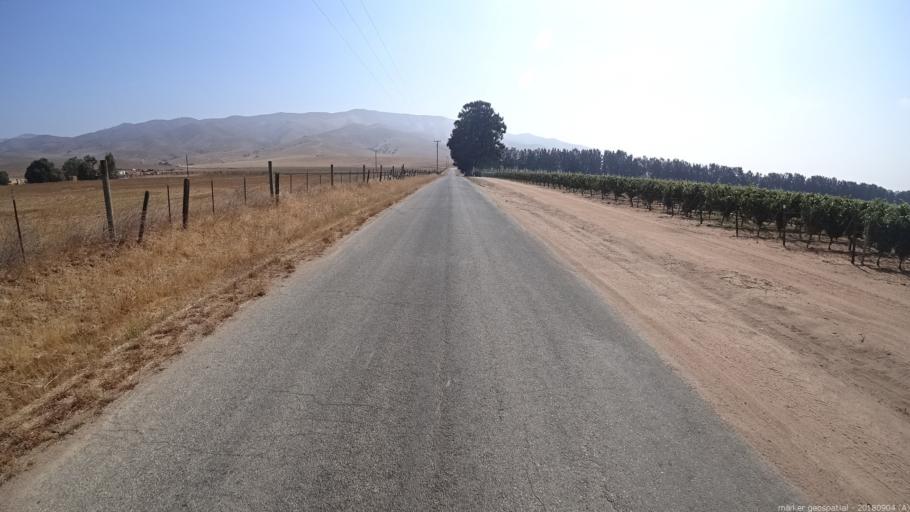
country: US
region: California
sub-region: Monterey County
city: Soledad
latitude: 36.4818
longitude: -121.3549
